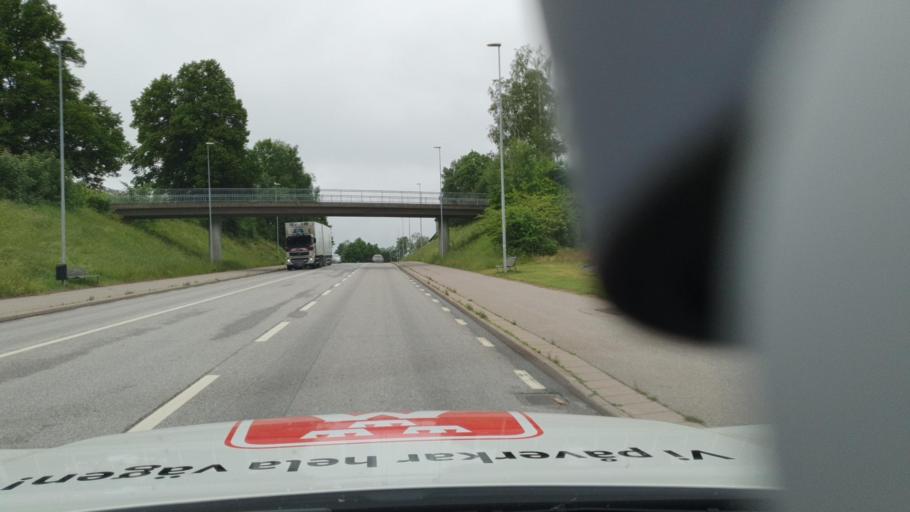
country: SE
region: OErebro
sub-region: Degerfors Kommun
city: Degerfors
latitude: 59.2391
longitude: 14.4340
